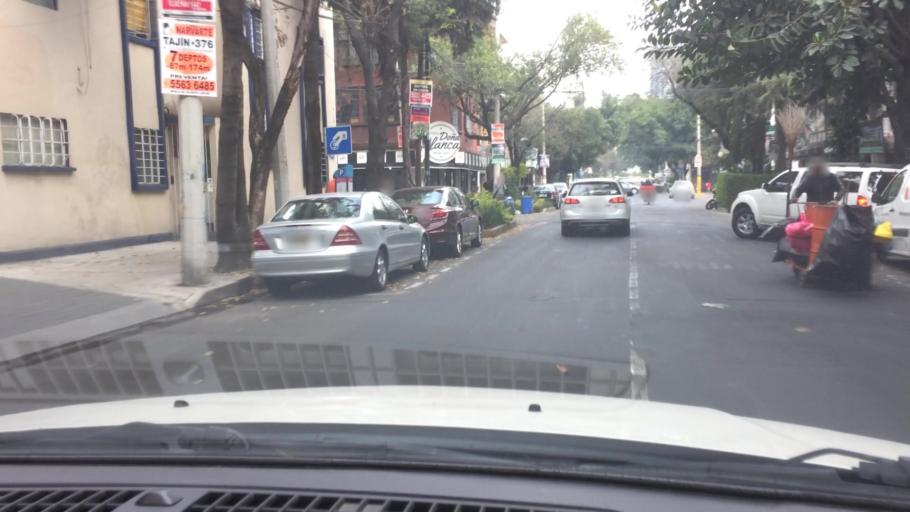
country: MX
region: Mexico City
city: Colonia del Valle
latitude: 19.3969
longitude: -99.1736
